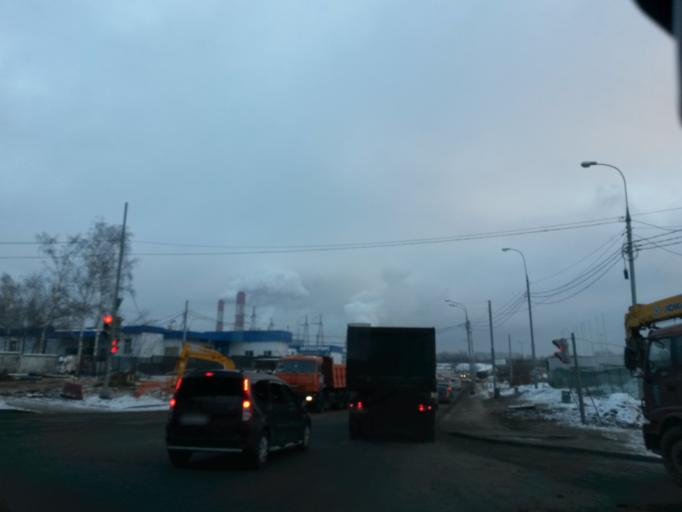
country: RU
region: Moscow
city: Mikhalkovo
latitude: 55.6874
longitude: 37.4290
